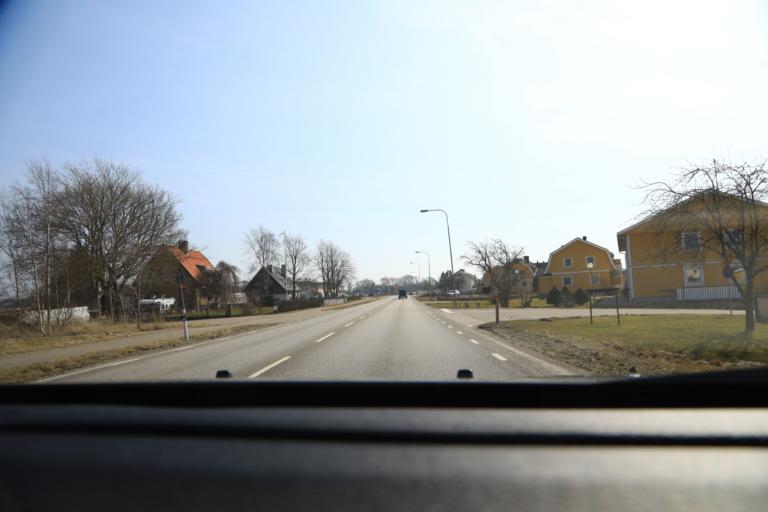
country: SE
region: Halland
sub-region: Kungsbacka Kommun
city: Frillesas
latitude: 57.2518
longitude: 12.1812
